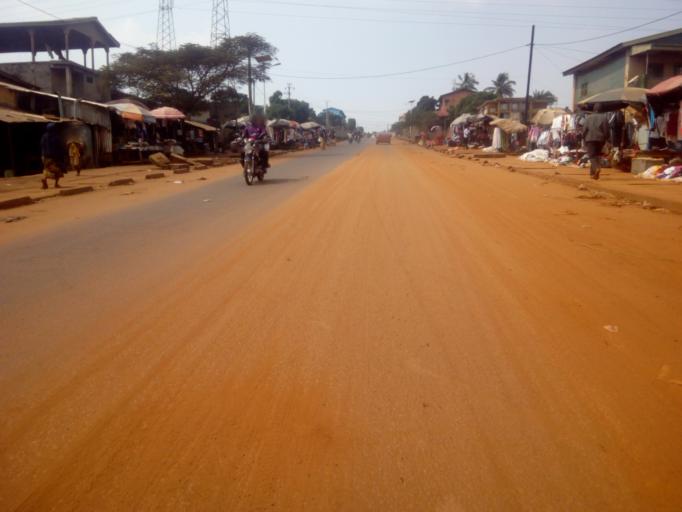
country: GN
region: Conakry
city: Conakry
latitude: 9.6348
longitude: -13.5728
